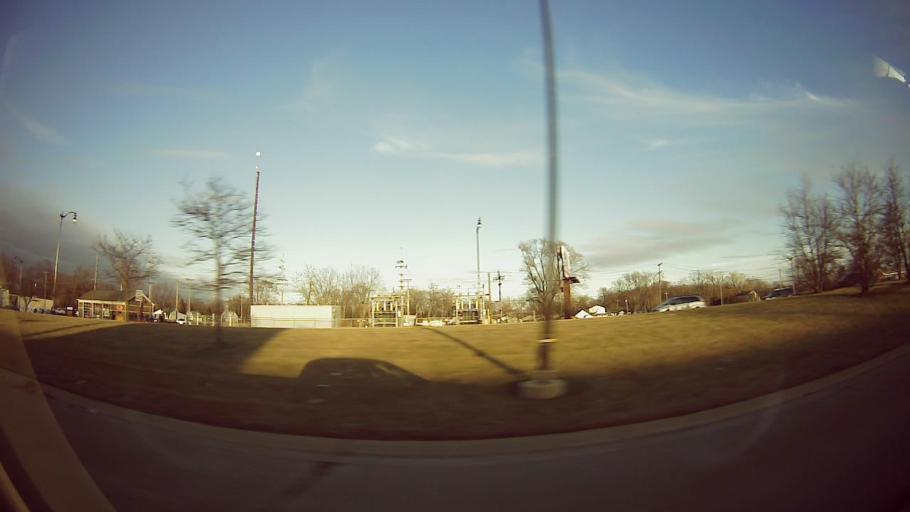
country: US
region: Michigan
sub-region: Wayne County
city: Taylor
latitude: 42.2207
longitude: -83.2692
